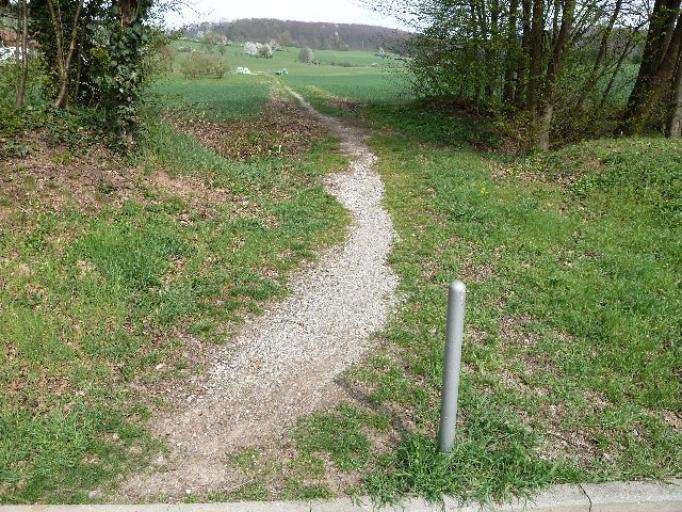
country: DE
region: Baden-Wuerttemberg
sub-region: Karlsruhe Region
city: Obrigheim
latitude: 49.3731
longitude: 9.0833
